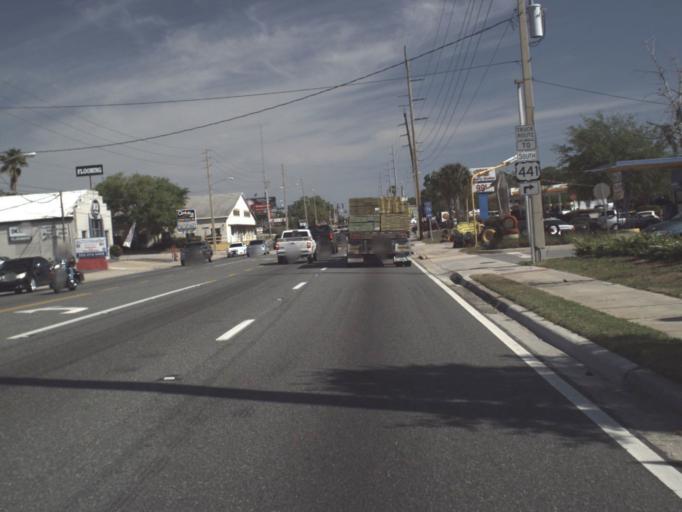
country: US
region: Florida
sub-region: Lake County
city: Leesburg
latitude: 28.8007
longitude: -81.8876
